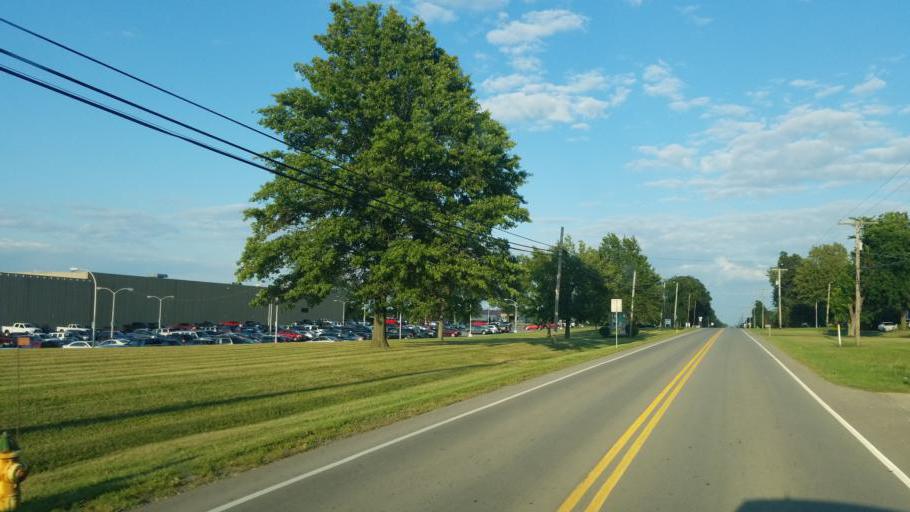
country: US
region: Ohio
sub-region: Huron County
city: Willard
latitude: 41.0529
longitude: -82.7094
